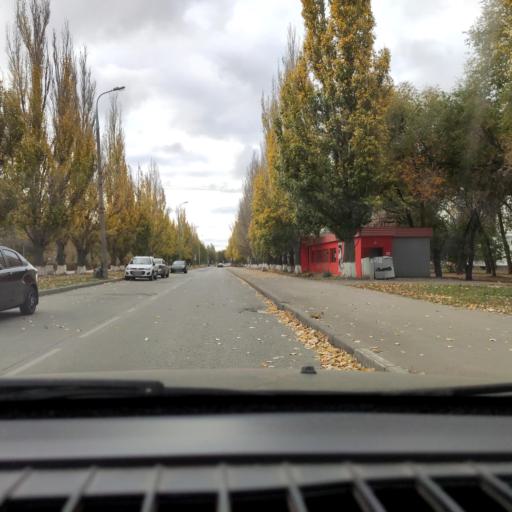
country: RU
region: Samara
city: Tol'yatti
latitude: 53.5338
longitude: 49.2671
